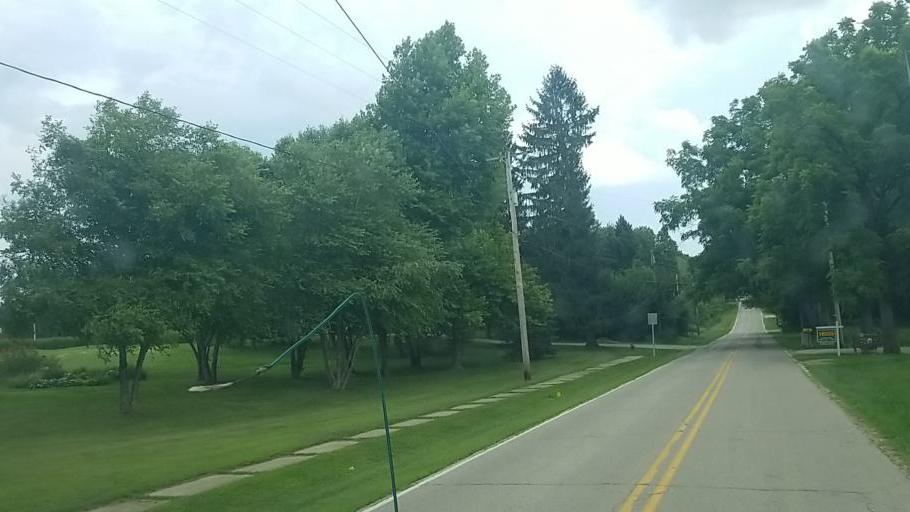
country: US
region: Ohio
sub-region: Medina County
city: Westfield Center
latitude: 41.0204
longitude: -81.9332
